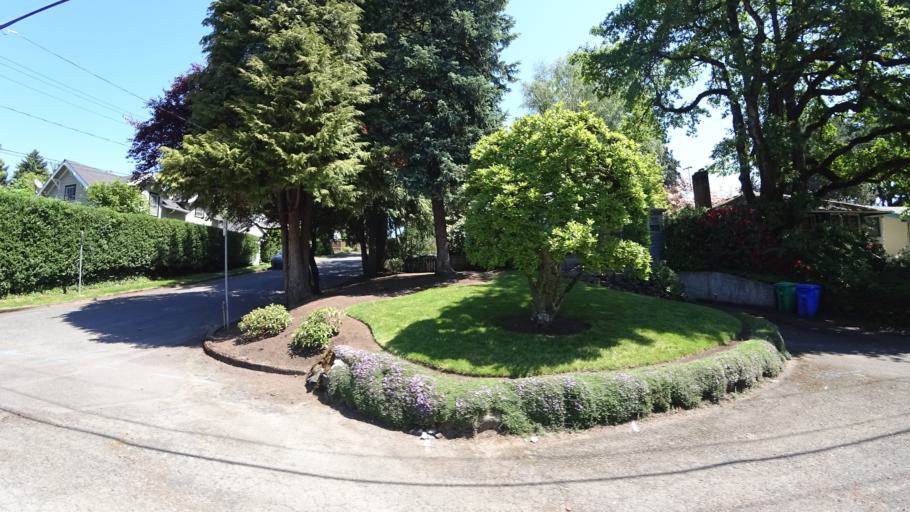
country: US
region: Oregon
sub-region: Multnomah County
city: Portland
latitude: 45.4732
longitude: -122.6835
